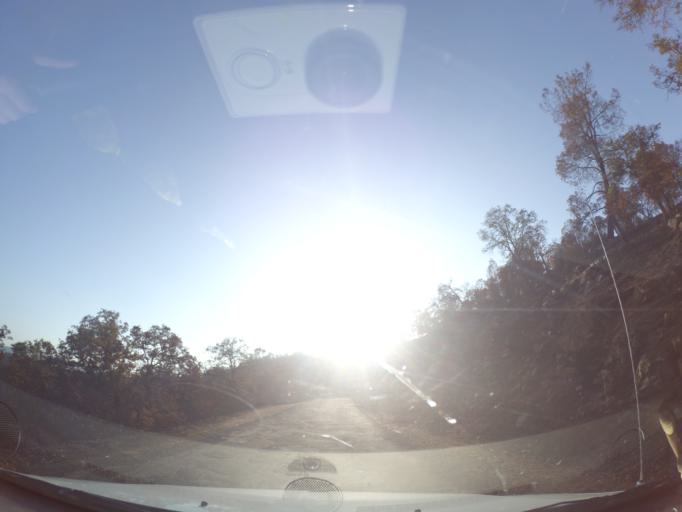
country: US
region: California
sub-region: Mariposa County
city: Mariposa
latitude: 37.5067
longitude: -120.0995
